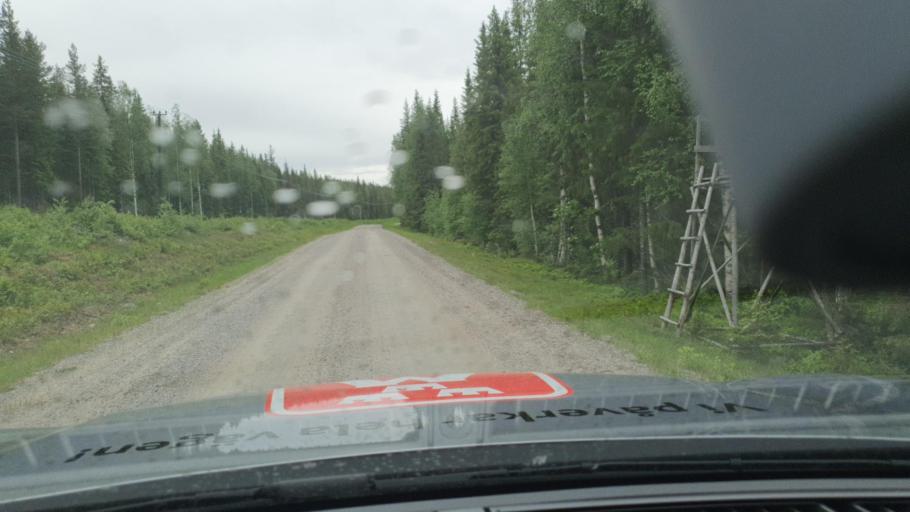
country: SE
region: Norrbotten
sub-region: Kalix Kommun
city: Rolfs
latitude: 66.0614
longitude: 23.0223
